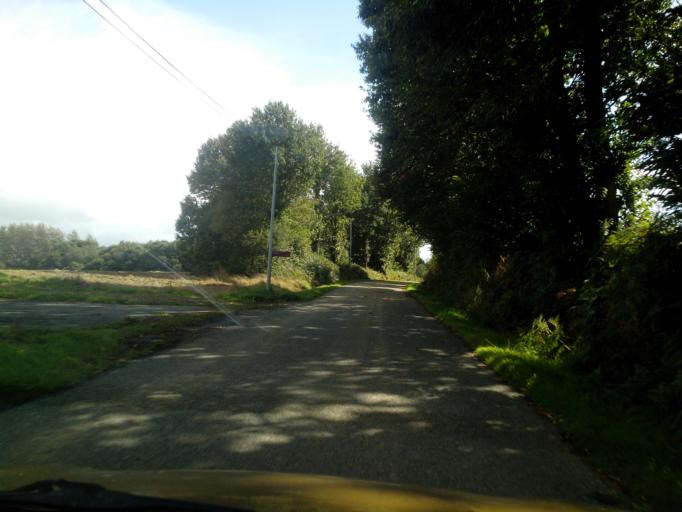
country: FR
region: Brittany
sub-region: Departement des Cotes-d'Armor
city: Merdrignac
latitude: 48.1526
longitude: -2.4137
